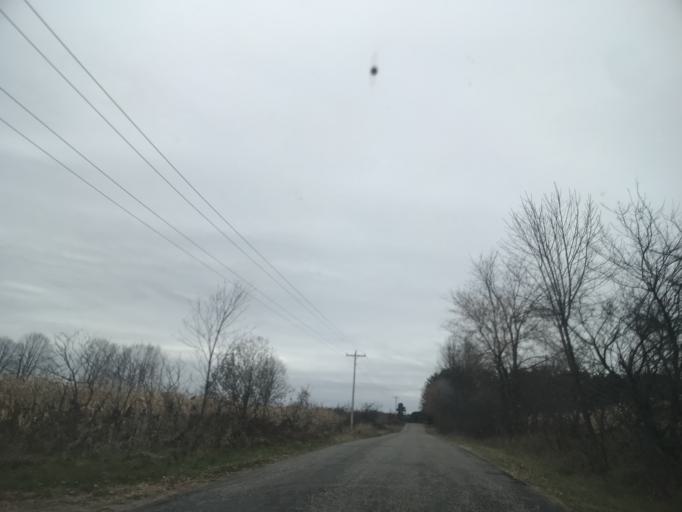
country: US
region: Wisconsin
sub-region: Menominee County
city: Legend Lake
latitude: 45.1768
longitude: -88.4554
